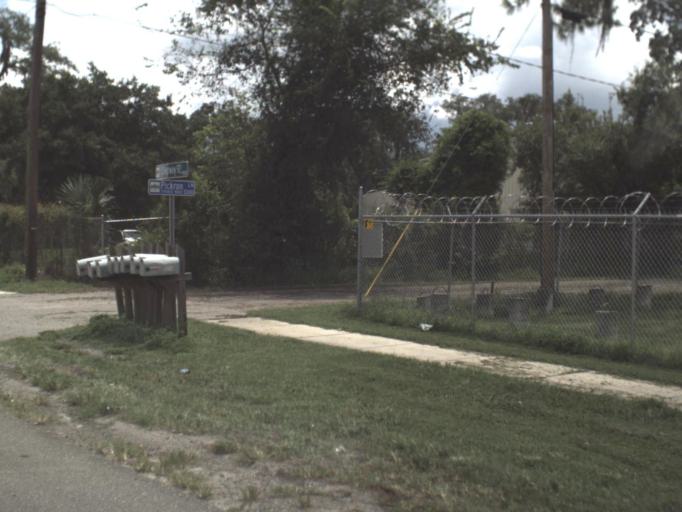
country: US
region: Florida
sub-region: Hillsborough County
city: Mango
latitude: 27.9951
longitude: -82.3380
